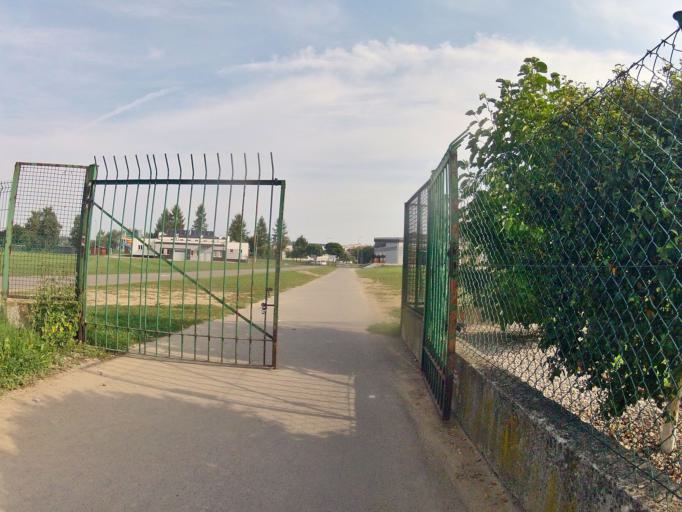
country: PL
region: Subcarpathian Voivodeship
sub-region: Powiat jasielski
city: Jaslo
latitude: 49.7425
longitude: 21.4564
